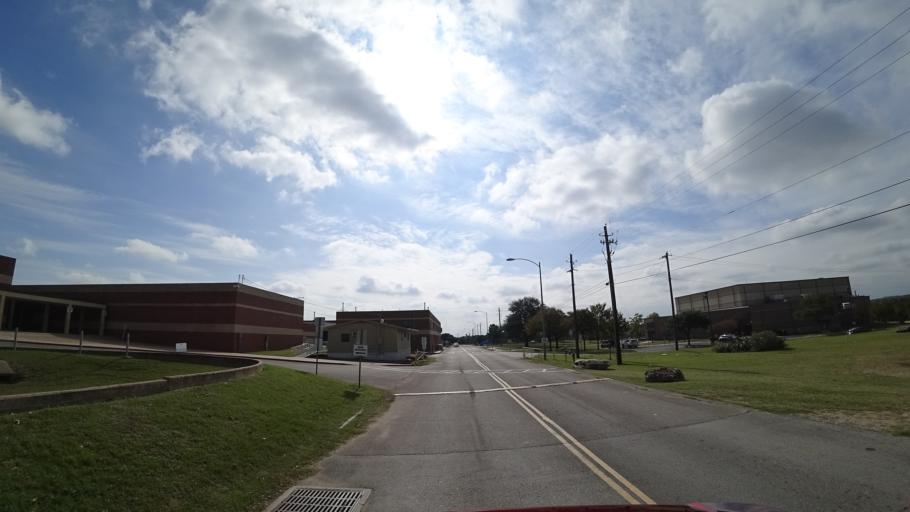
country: US
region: Texas
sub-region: Williamson County
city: Jollyville
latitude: 30.4489
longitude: -97.7353
